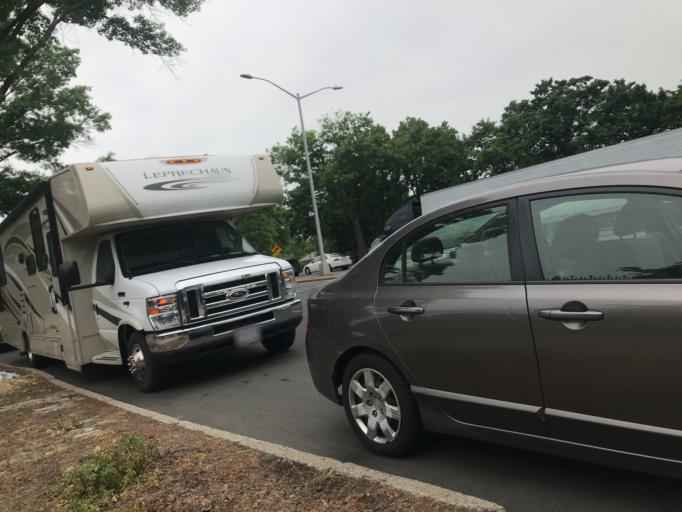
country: US
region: New York
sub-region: Queens County
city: Jamaica
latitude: 40.7492
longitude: -73.8327
